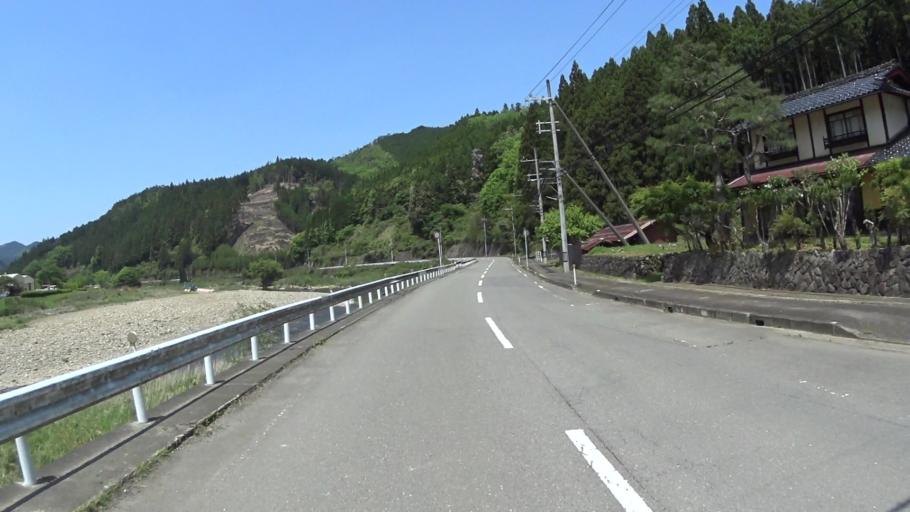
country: JP
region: Kyoto
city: Kameoka
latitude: 35.1366
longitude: 135.6034
